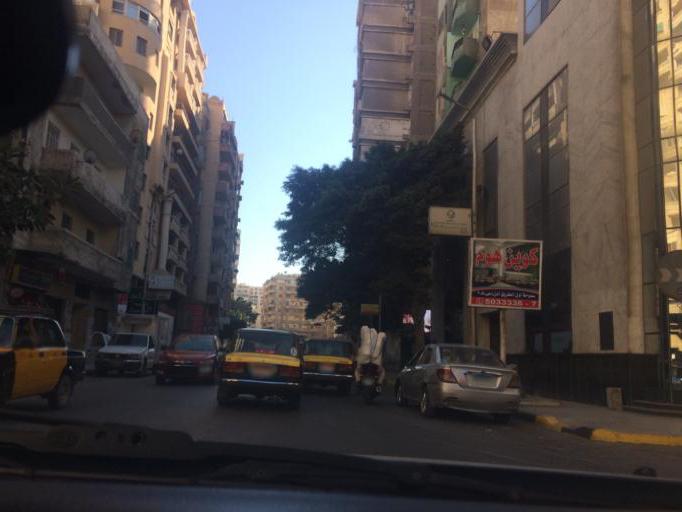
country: EG
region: Alexandria
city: Alexandria
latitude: 31.2392
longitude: 29.9637
